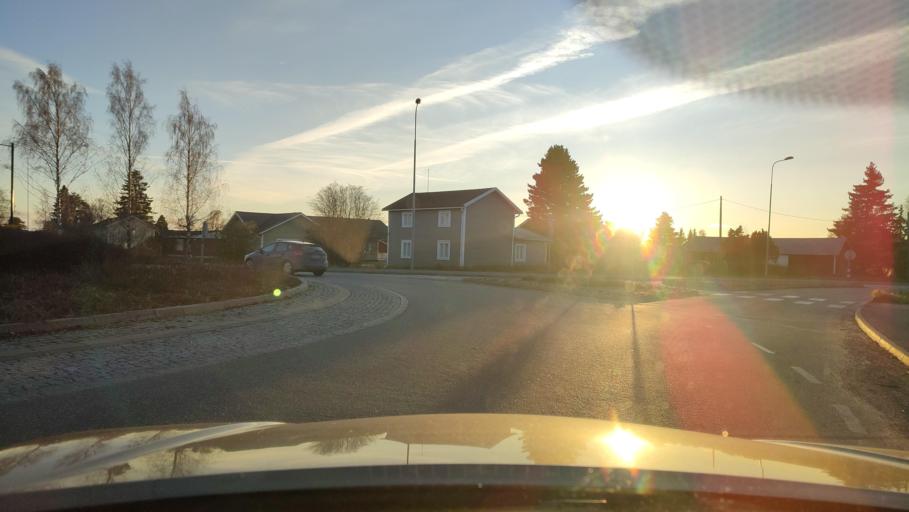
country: FI
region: Ostrobothnia
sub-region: Sydosterbotten
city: Naerpes
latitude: 62.4834
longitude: 21.3379
